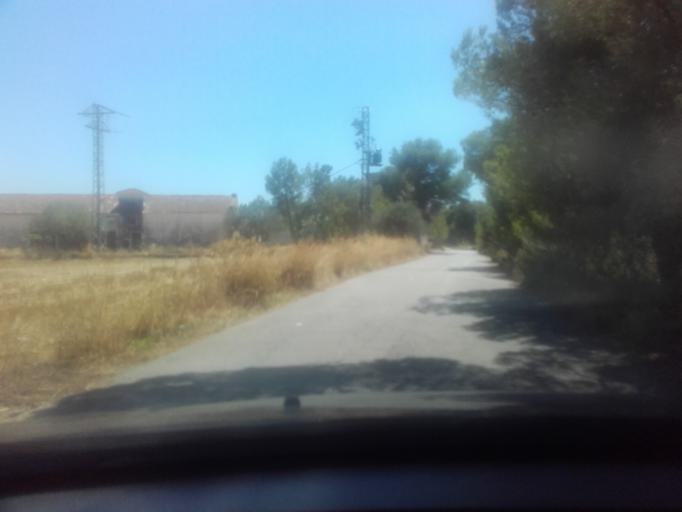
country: ES
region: Catalonia
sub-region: Provincia de Tarragona
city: Santa Oliva
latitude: 41.2579
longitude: 1.5285
